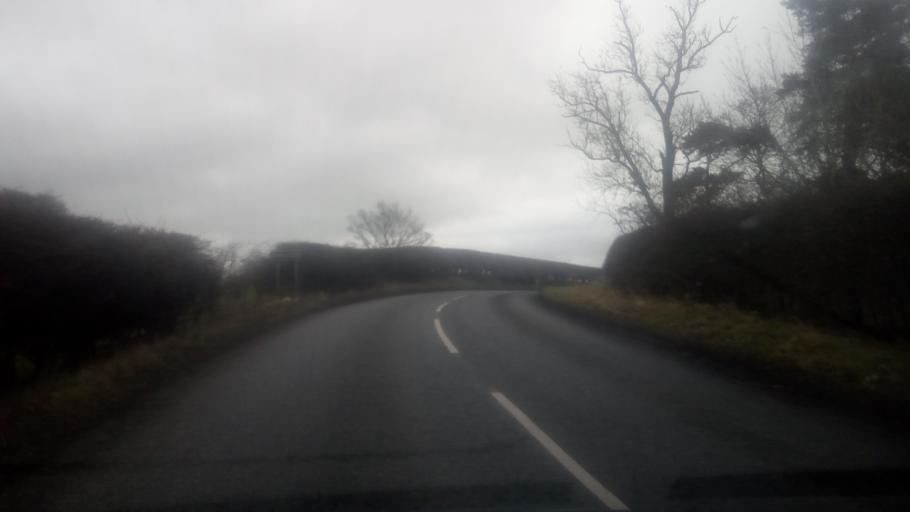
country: GB
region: Scotland
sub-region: The Scottish Borders
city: Kelso
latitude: 55.5986
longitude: -2.4528
